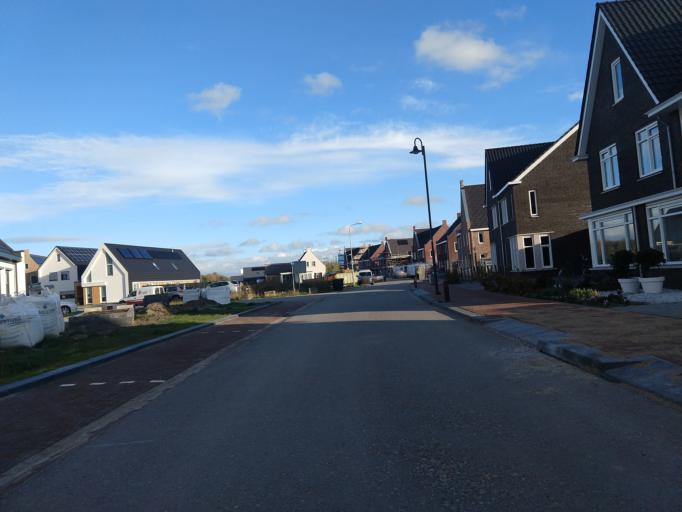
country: NL
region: Zeeland
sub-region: Gemeente Goes
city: Goes
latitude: 51.5184
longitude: 3.8958
